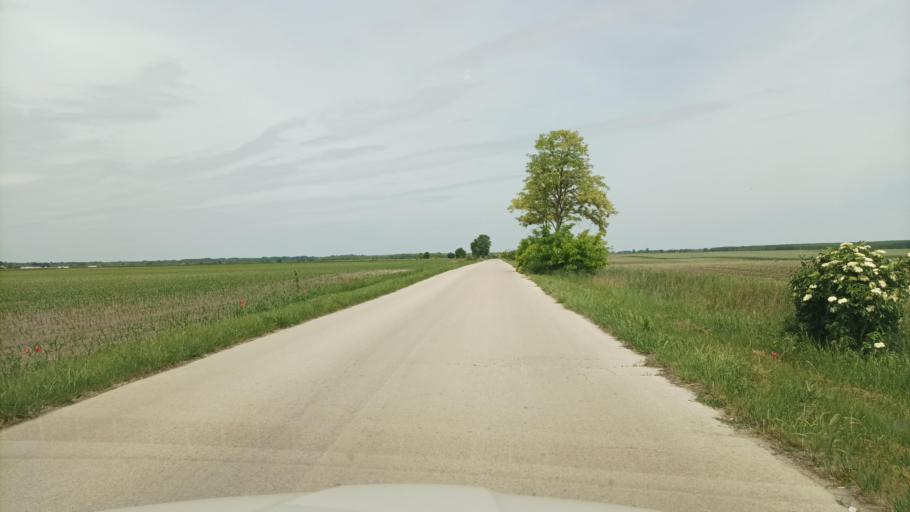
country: HU
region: Pest
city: Rackeve
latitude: 47.1069
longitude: 18.9260
